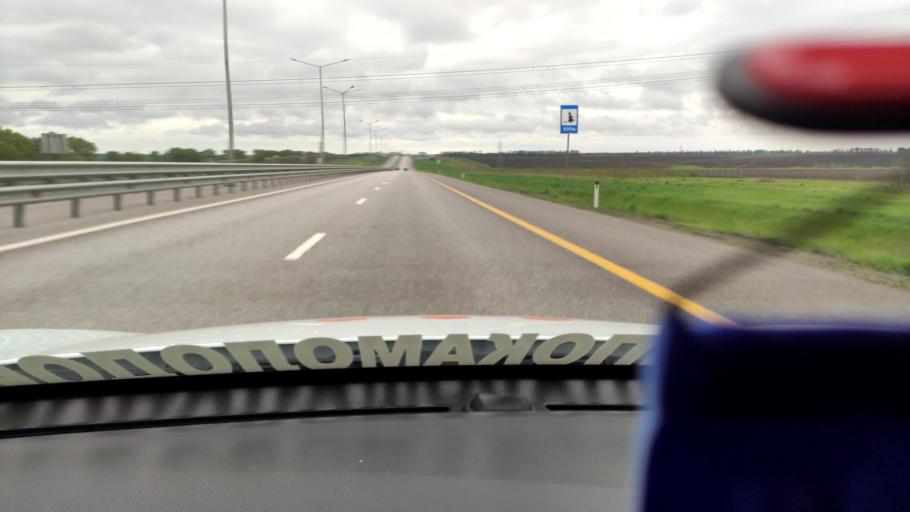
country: RU
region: Voronezj
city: Podkletnoye
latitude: 51.5499
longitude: 39.4921
